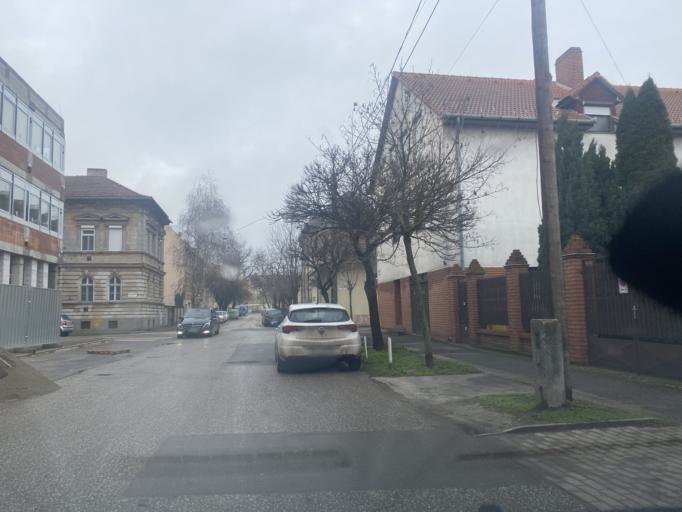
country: HU
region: Csongrad
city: Szeged
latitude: 46.2622
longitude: 20.1403
